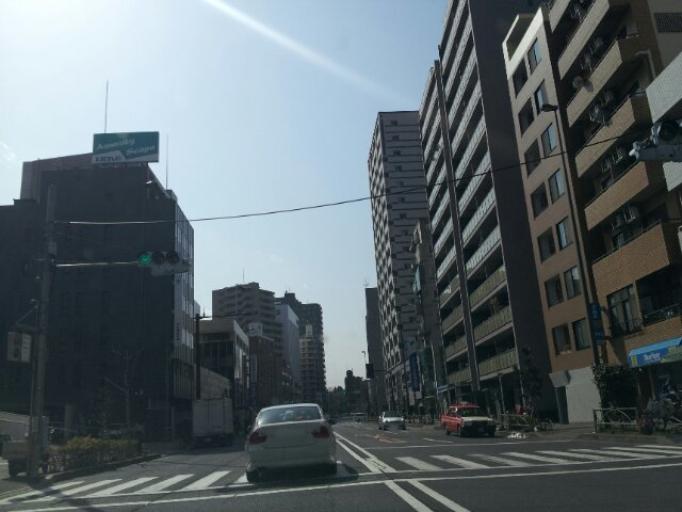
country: JP
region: Tokyo
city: Tokyo
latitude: 35.6447
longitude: 139.7375
